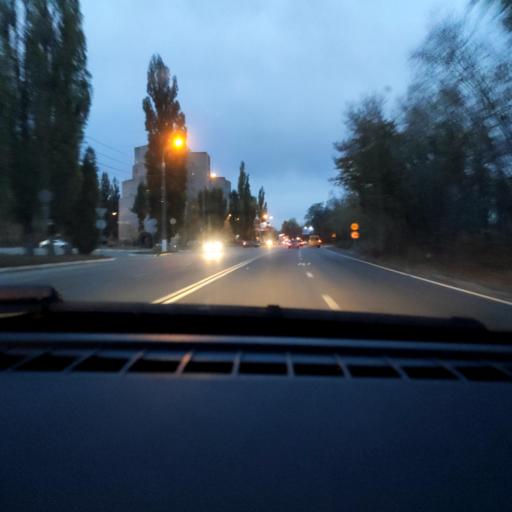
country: RU
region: Voronezj
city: Maslovka
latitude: 51.6018
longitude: 39.2535
